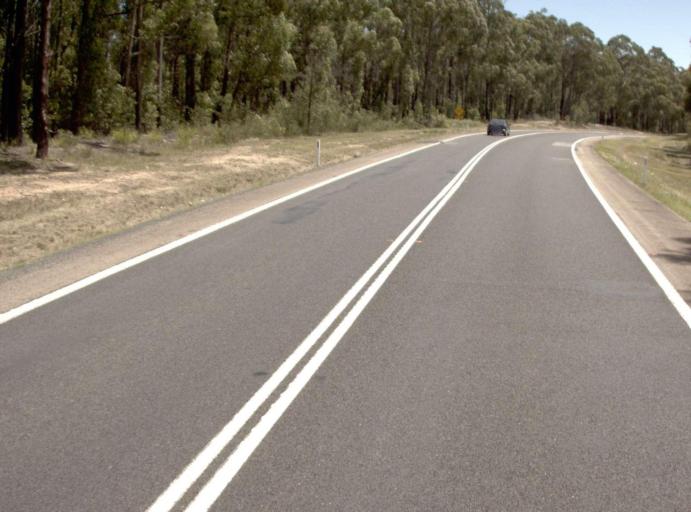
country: AU
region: New South Wales
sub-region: Bombala
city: Bombala
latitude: -37.5667
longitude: 149.1137
